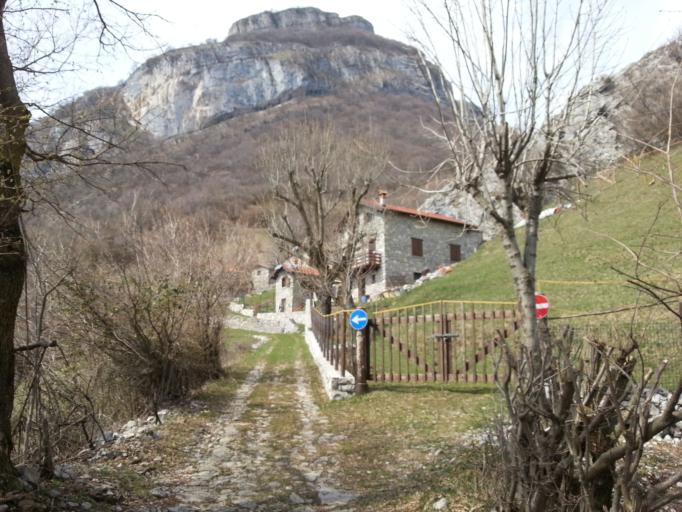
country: IT
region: Lombardy
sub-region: Provincia di Como
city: Tremezzo
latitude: 46.0018
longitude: 9.2082
